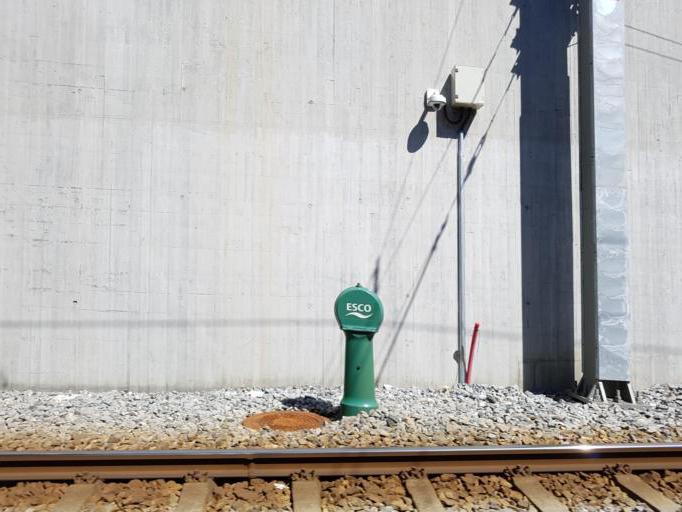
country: NO
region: Hordaland
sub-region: Bergen
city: Sandsli
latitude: 60.3001
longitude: 5.3112
